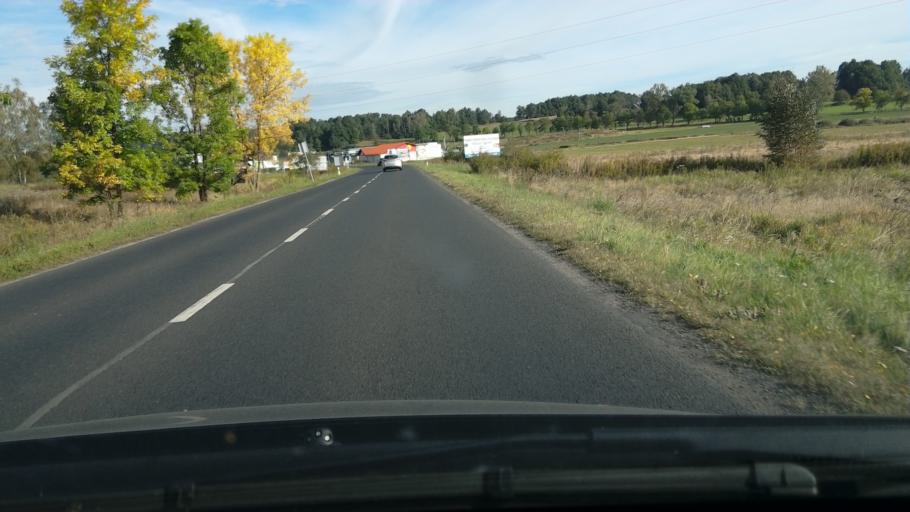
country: PL
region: Lower Silesian Voivodeship
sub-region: Powiat jeleniogorski
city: Myslakowice
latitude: 50.8537
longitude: 15.7742
